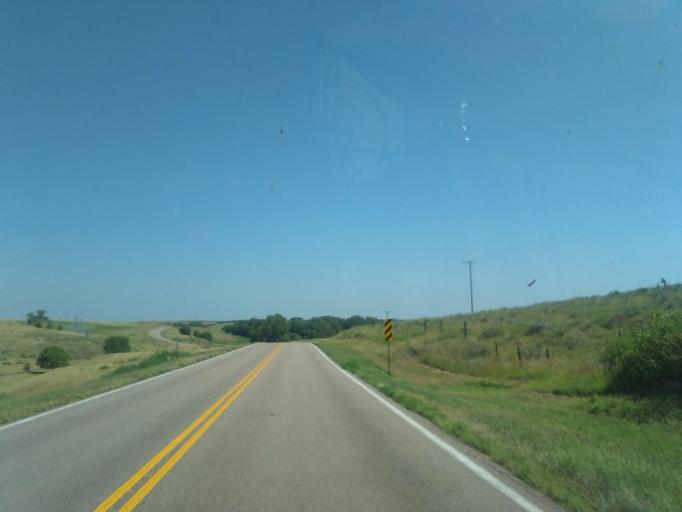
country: US
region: Nebraska
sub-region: Dundy County
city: Benkelman
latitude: 39.8835
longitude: -101.5411
